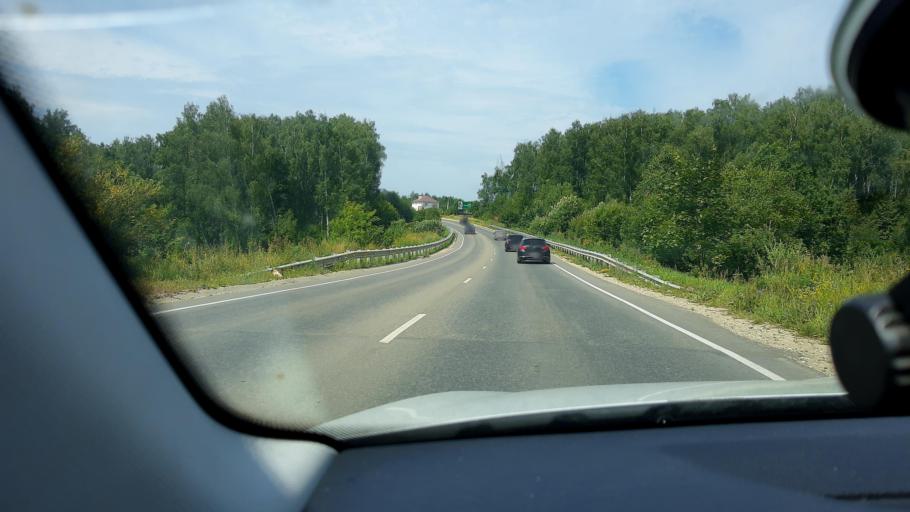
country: RU
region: Tula
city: Zaokskiy
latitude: 54.7432
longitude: 37.4173
